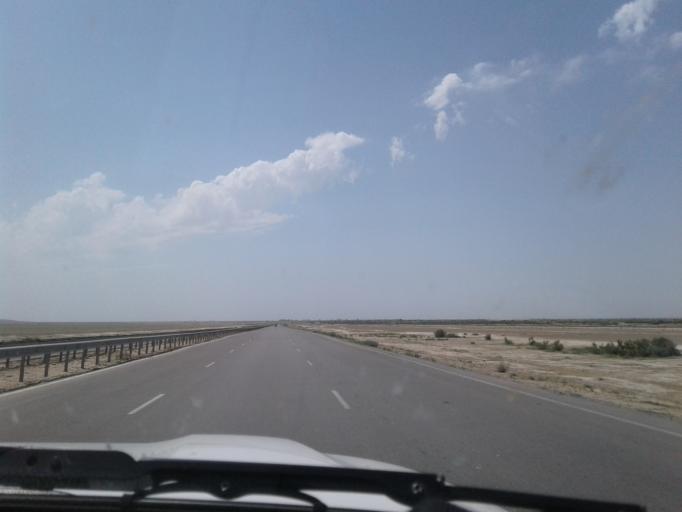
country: IR
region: Razavi Khorasan
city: Dargaz
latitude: 37.7303
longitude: 58.9942
